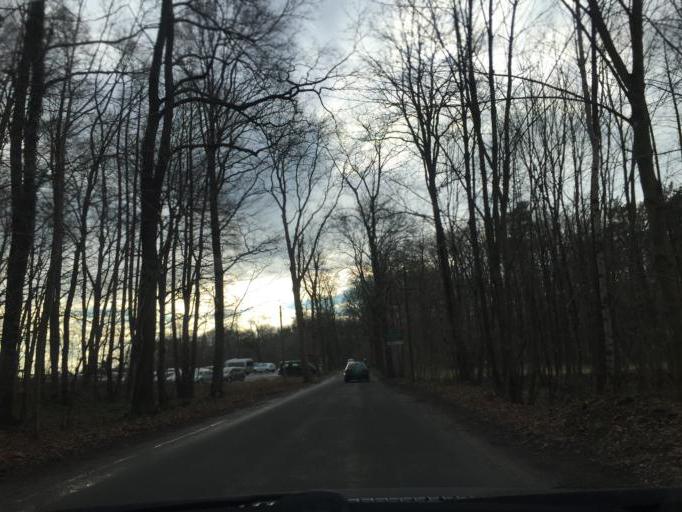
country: DE
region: Saxony
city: Moritzburg
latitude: 51.1707
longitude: 13.6743
